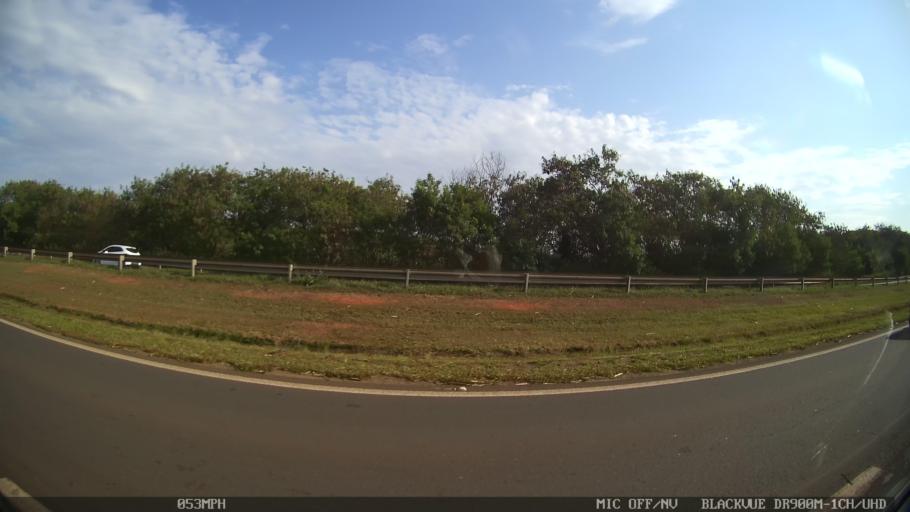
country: BR
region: Sao Paulo
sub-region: Cosmopolis
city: Cosmopolis
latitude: -22.6589
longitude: -47.1710
